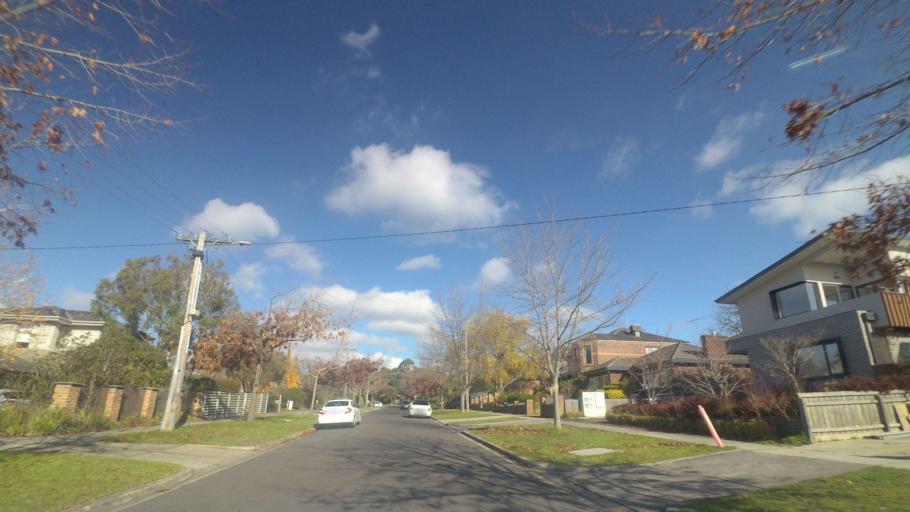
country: AU
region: Victoria
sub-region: Whitehorse
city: Mont Albert North
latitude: -37.8077
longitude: 145.1039
